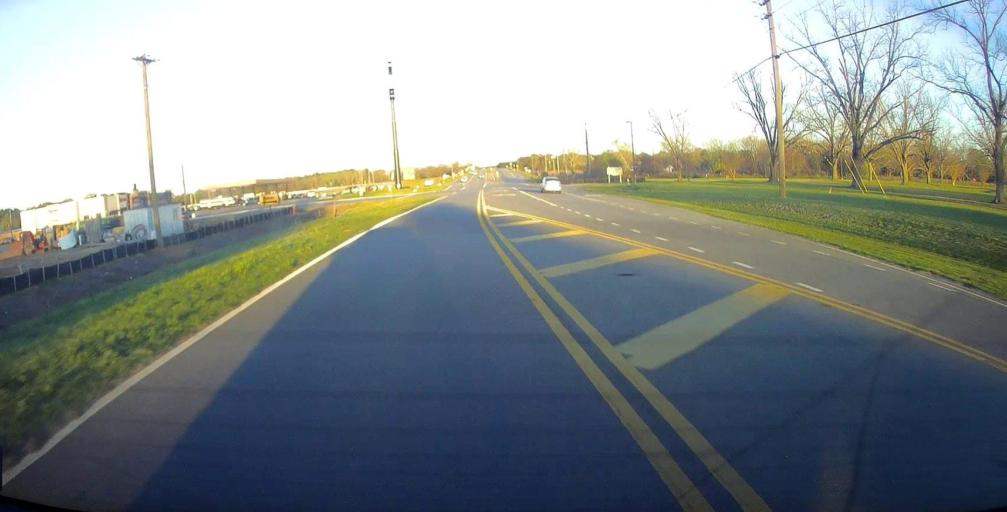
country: US
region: Georgia
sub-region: Crisp County
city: Cordele
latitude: 31.9750
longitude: -83.7597
